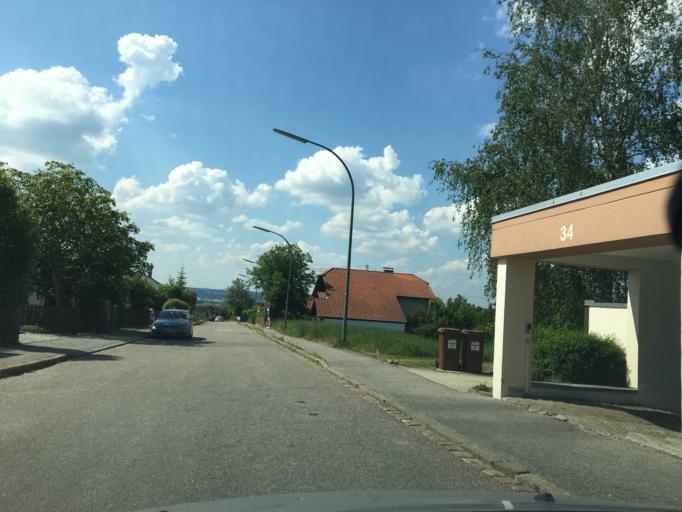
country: DE
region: Bavaria
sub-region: Lower Bavaria
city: Landshut
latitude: 48.5208
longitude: 12.1538
